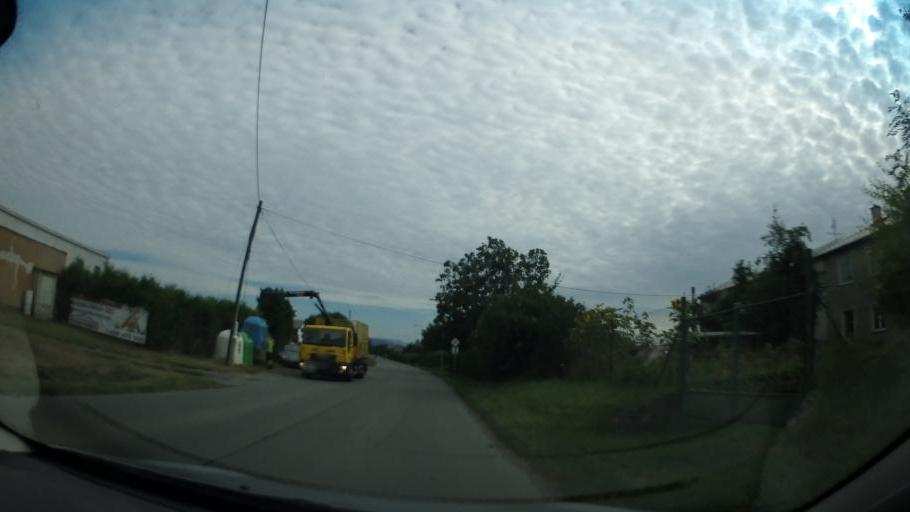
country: CZ
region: Olomoucky
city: Zabreh
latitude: 49.8873
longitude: 16.8772
